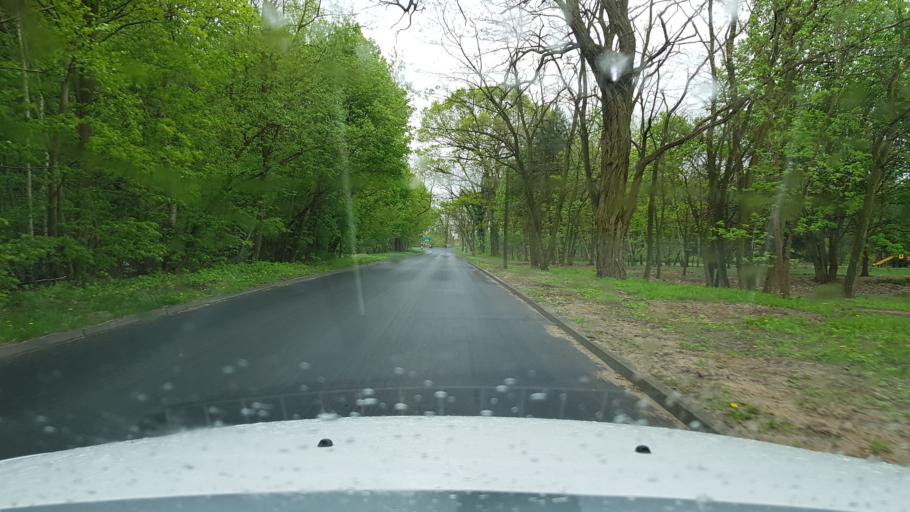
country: PL
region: West Pomeranian Voivodeship
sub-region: Powiat mysliborski
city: Debno
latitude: 52.7438
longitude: 14.7116
